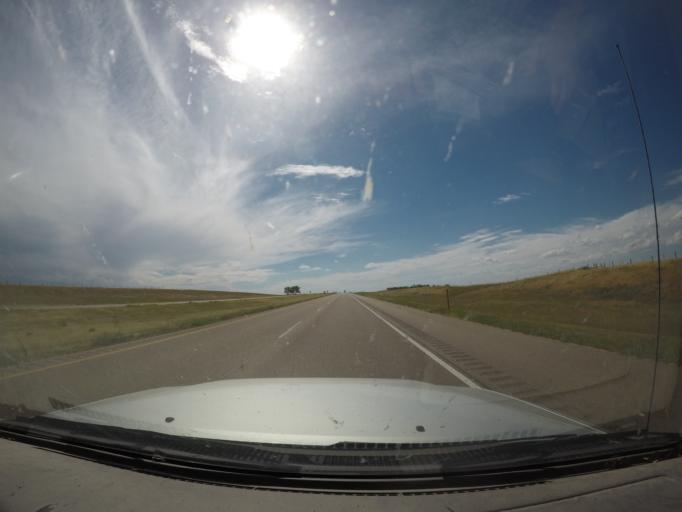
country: US
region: Colorado
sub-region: Sedgwick County
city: Julesburg
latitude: 41.0484
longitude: -102.3419
